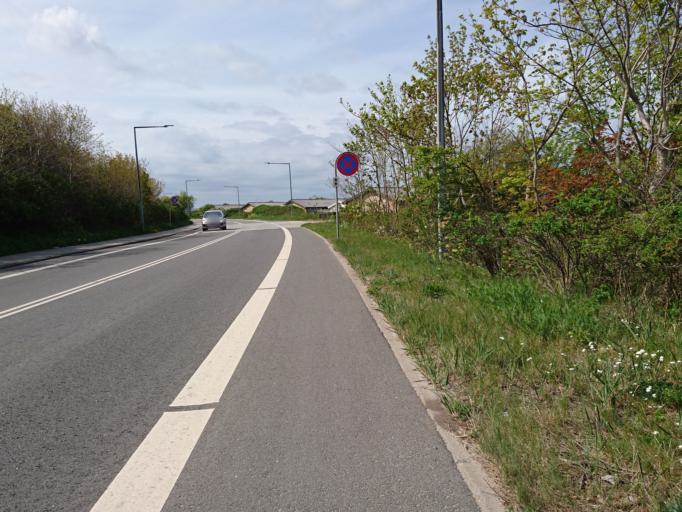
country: DK
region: North Denmark
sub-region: Frederikshavn Kommune
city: Skagen
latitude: 57.7285
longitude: 10.5587
